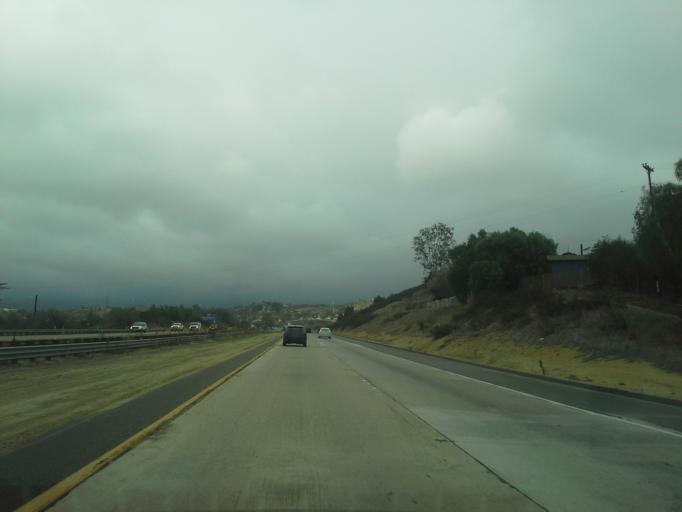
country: US
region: California
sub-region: San Diego County
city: Granite Hills
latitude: 32.8372
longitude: -116.8907
